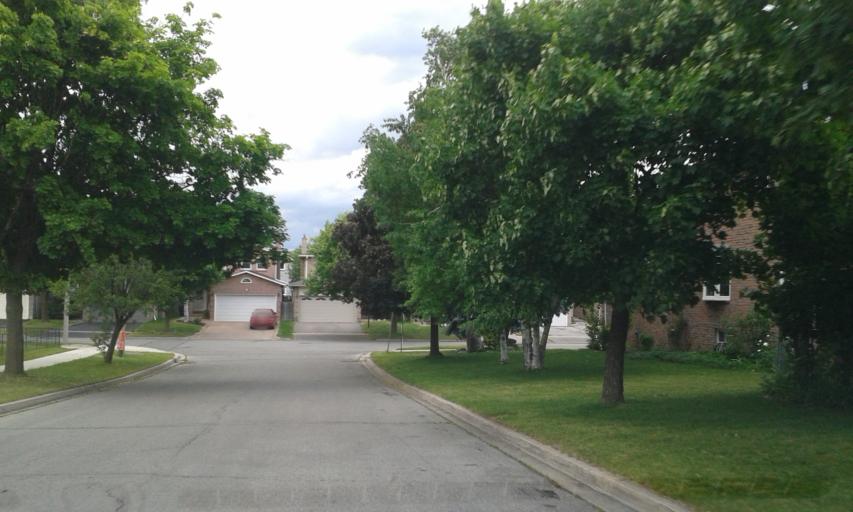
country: CA
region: Ontario
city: Scarborough
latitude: 43.8105
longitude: -79.2614
